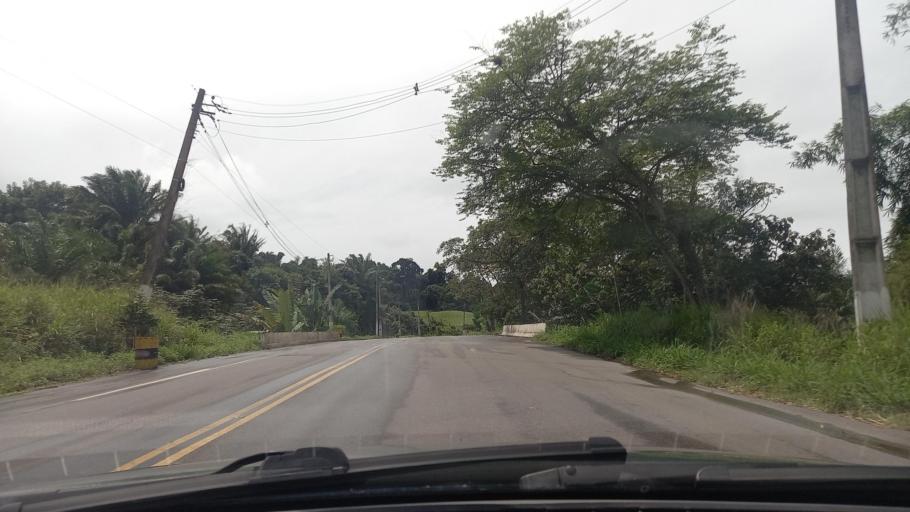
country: BR
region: Alagoas
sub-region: Sao Miguel Dos Campos
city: Sao Miguel dos Campos
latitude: -9.8098
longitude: -36.2204
